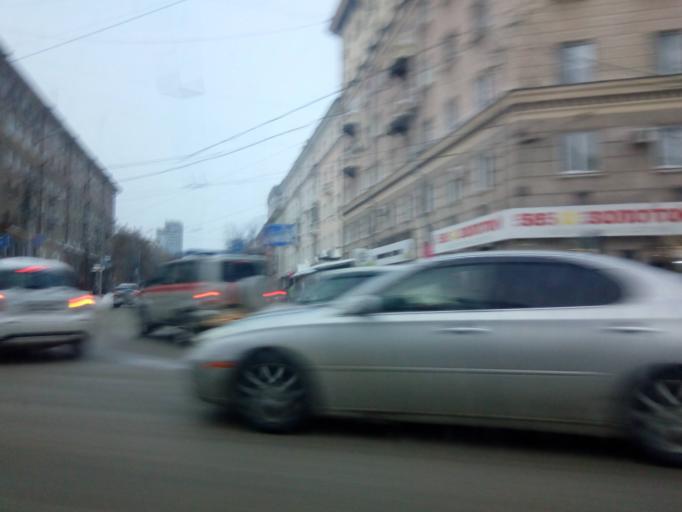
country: RU
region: Novosibirsk
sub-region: Novosibirskiy Rayon
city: Novosibirsk
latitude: 55.0305
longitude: 82.9158
